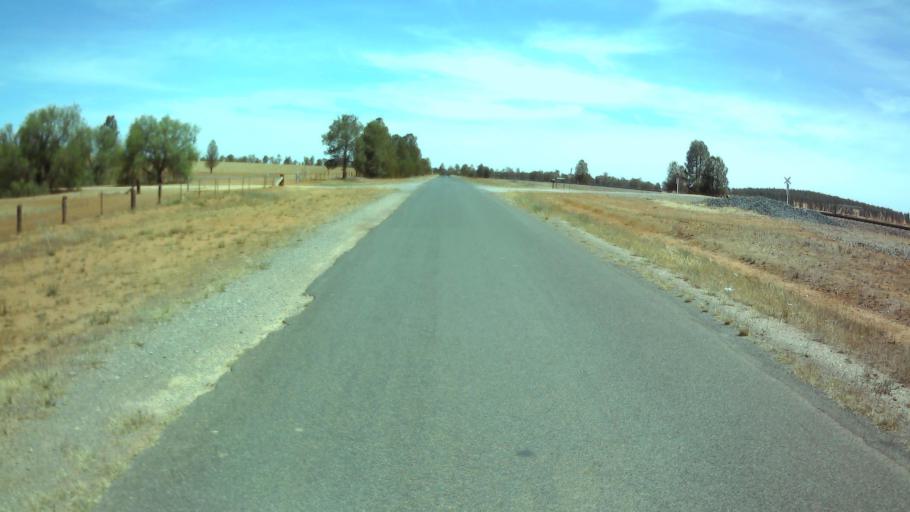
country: AU
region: New South Wales
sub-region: Weddin
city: Grenfell
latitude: -33.7729
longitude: 147.7561
